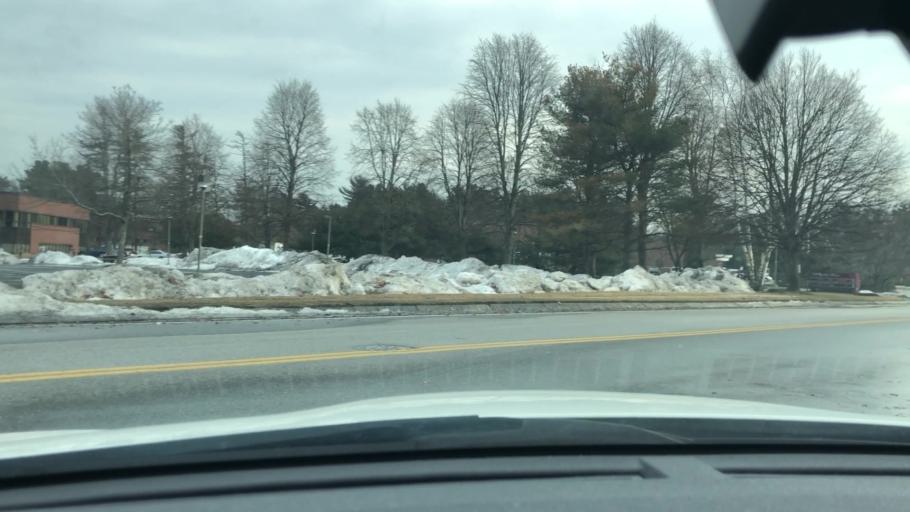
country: US
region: Massachusetts
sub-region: Middlesex County
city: Lowell
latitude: 42.6000
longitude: -71.3284
